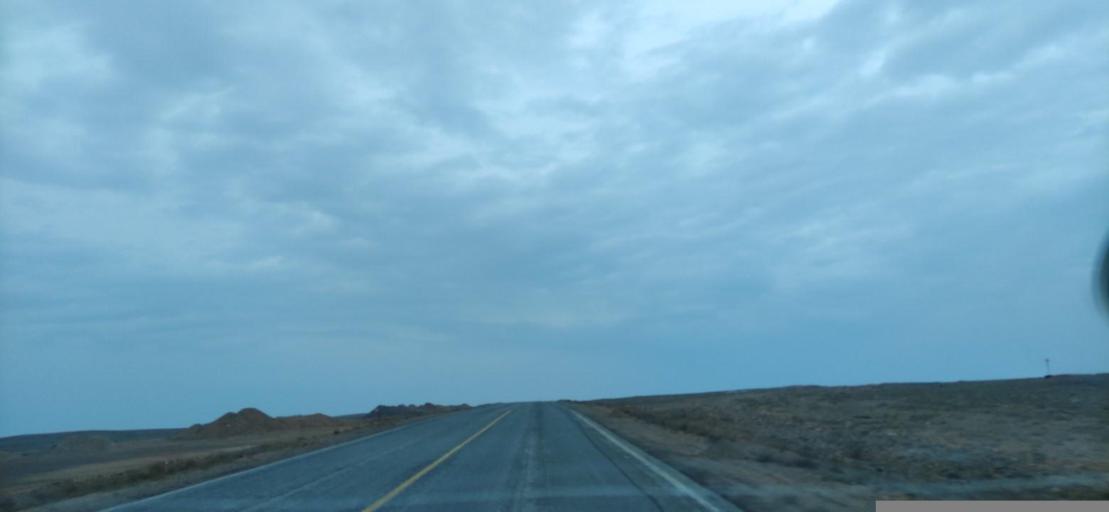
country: KZ
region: Qaraghandy
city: Saryshaghan
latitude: 46.3879
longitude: 73.8525
